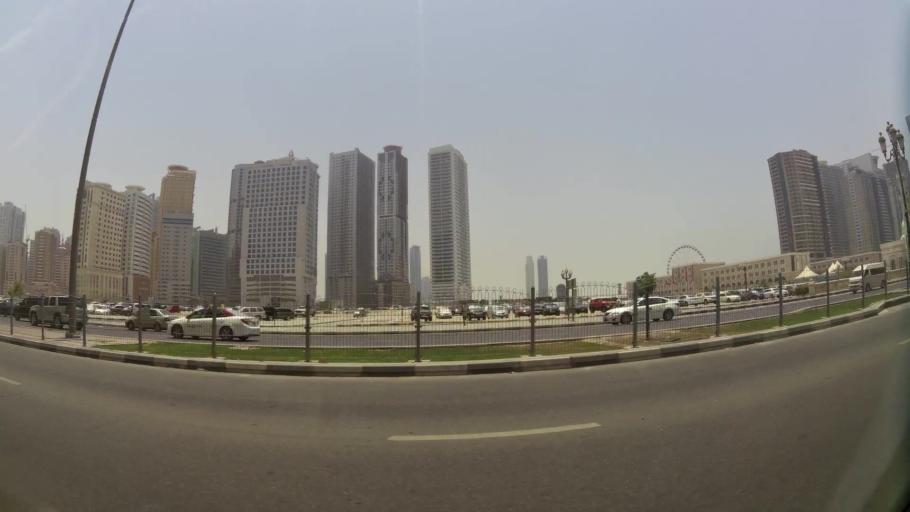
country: AE
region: Ash Shariqah
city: Sharjah
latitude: 25.3210
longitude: 55.3794
